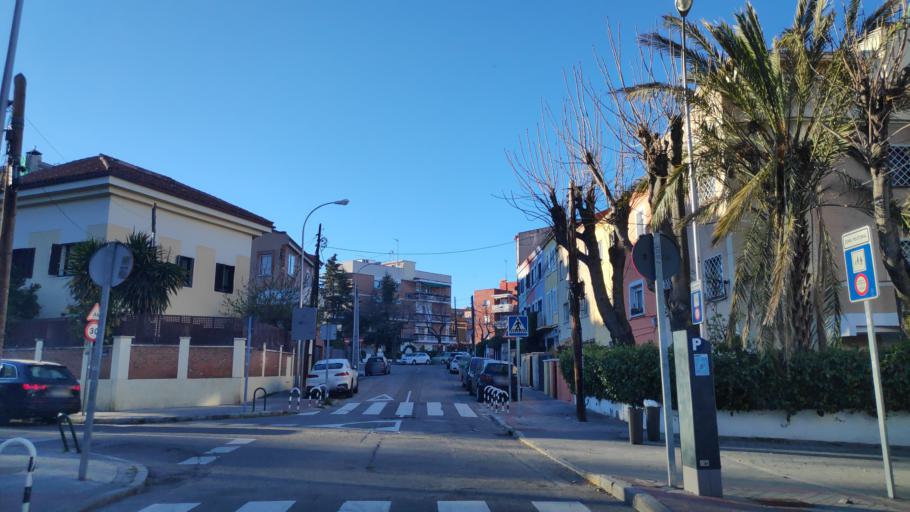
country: ES
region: Madrid
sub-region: Provincia de Madrid
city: Chamartin
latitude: 40.4508
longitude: -3.6686
